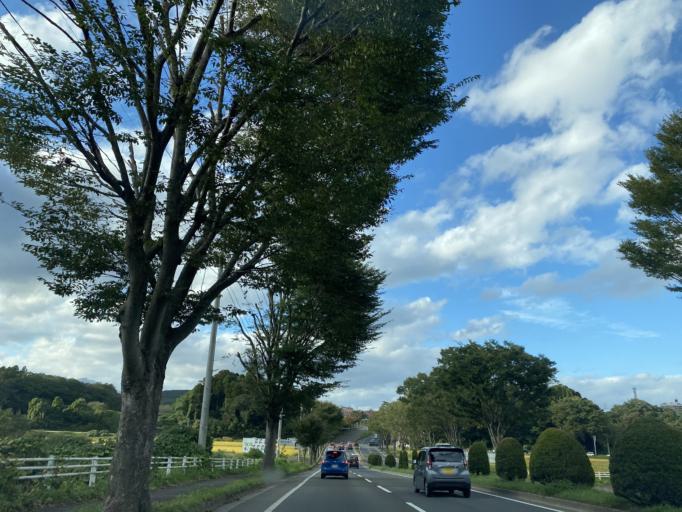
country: JP
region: Miyagi
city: Sendai-shi
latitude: 38.3268
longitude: 140.8428
